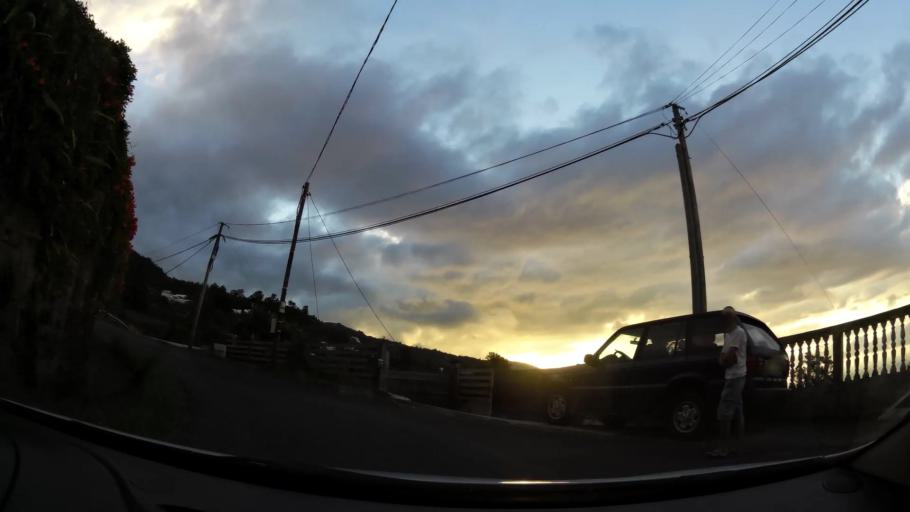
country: RE
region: Reunion
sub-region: Reunion
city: Saint-Denis
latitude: -20.9177
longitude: 55.4637
